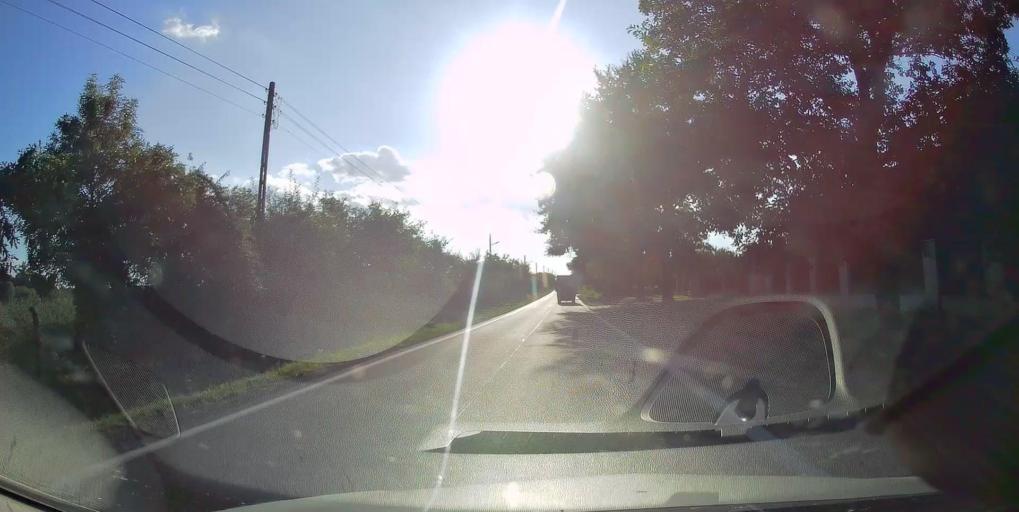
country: PL
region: Lodz Voivodeship
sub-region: Powiat rawski
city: Biala Rawska
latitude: 51.8080
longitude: 20.4927
